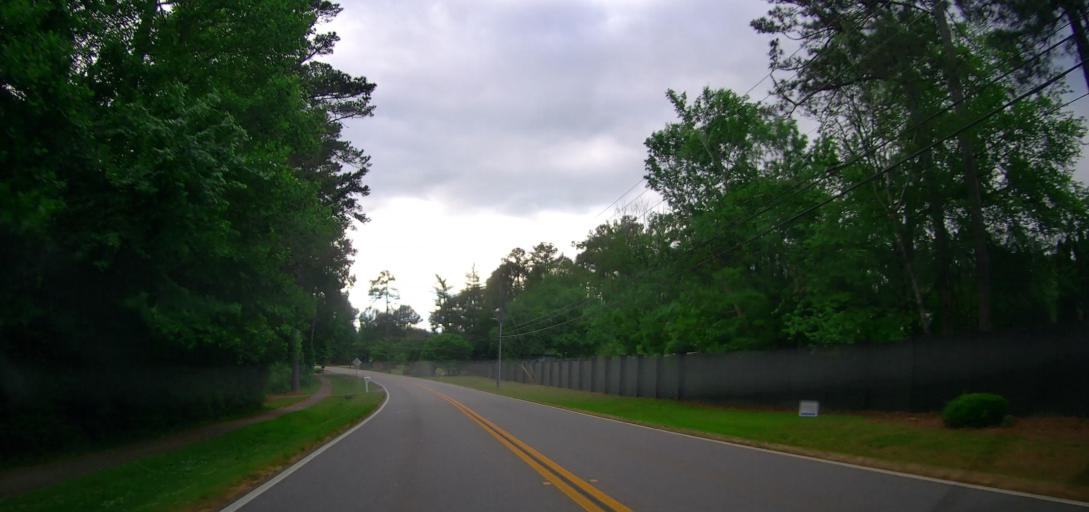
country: US
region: Georgia
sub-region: Clarke County
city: Athens
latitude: 33.9340
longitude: -83.4276
